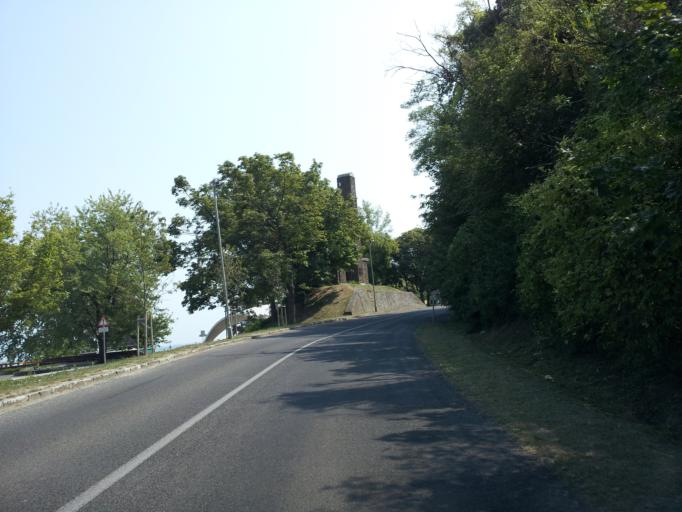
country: HU
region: Veszprem
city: Tihany
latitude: 46.9179
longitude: 17.8914
